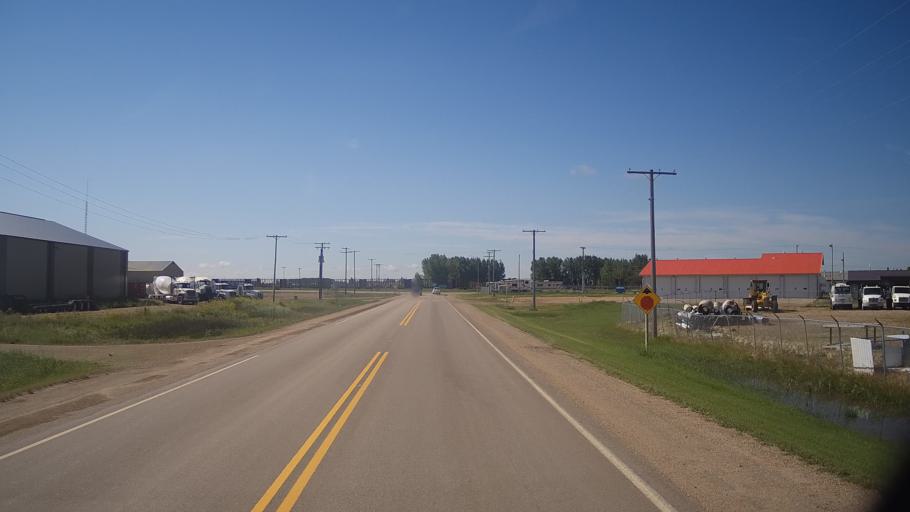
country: CA
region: Saskatchewan
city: Watrous
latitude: 51.6682
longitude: -105.4516
